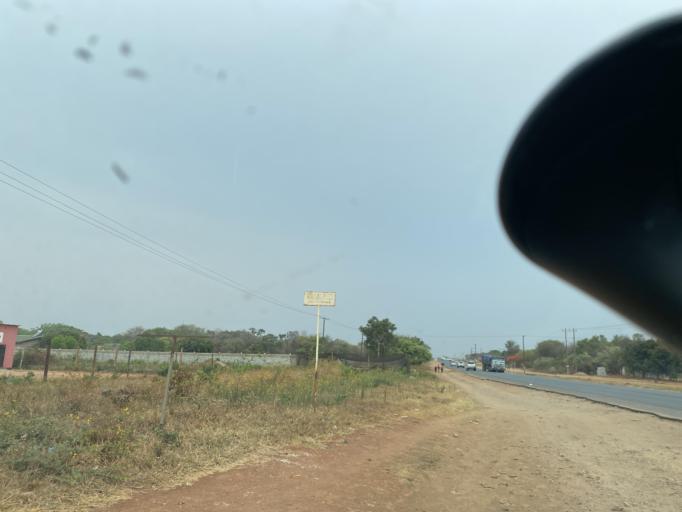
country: ZM
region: Lusaka
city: Lusaka
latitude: -15.2929
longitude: 28.2712
